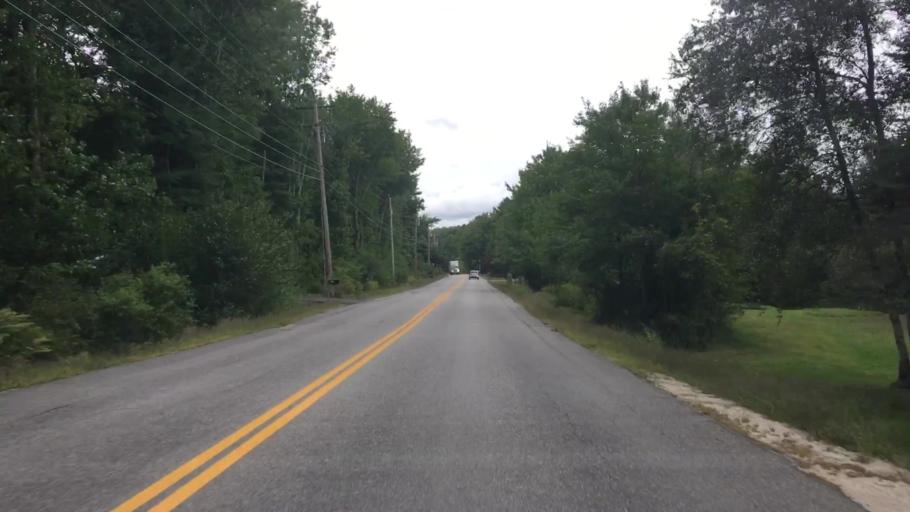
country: US
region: Maine
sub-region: Cumberland County
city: Yarmouth
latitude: 43.8340
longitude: -70.2027
